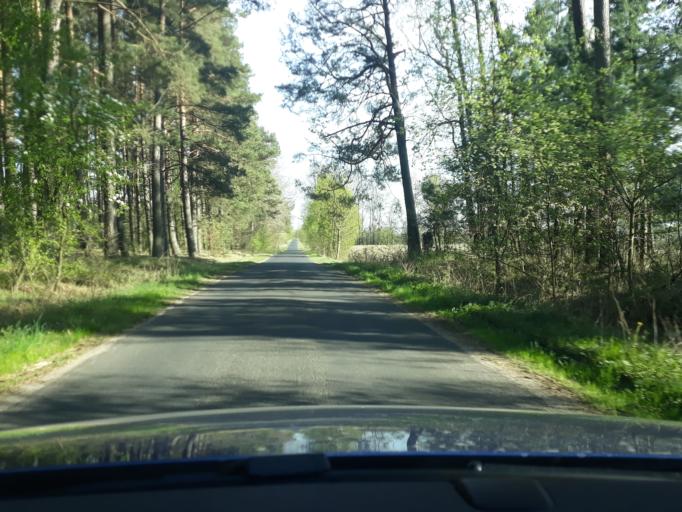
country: PL
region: Pomeranian Voivodeship
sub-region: Powiat czluchowski
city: Przechlewo
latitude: 53.8574
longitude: 17.3486
